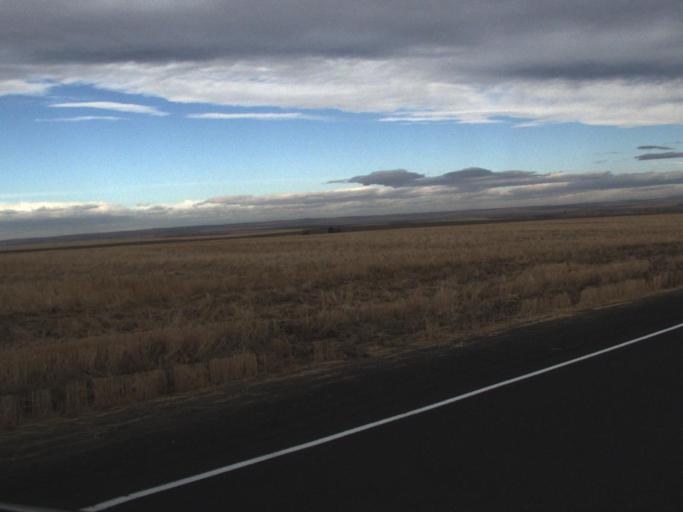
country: US
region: Washington
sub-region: Okanogan County
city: Coulee Dam
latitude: 47.6453
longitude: -118.7210
